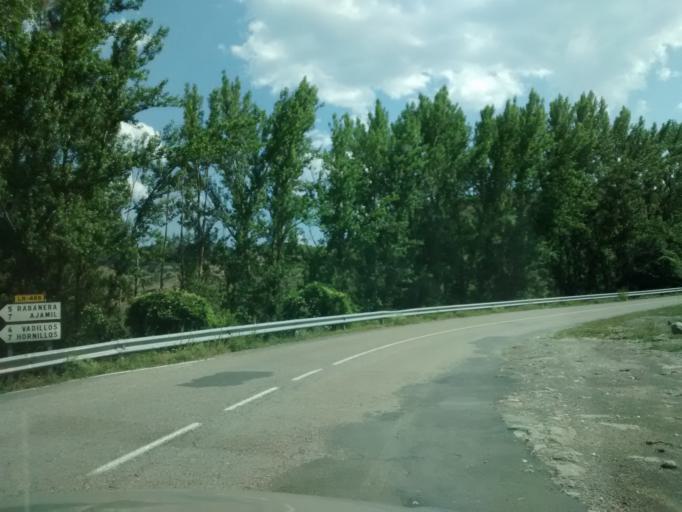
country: ES
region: La Rioja
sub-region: Provincia de La Rioja
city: Jalon de Cameros
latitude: 42.2210
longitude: -2.4803
